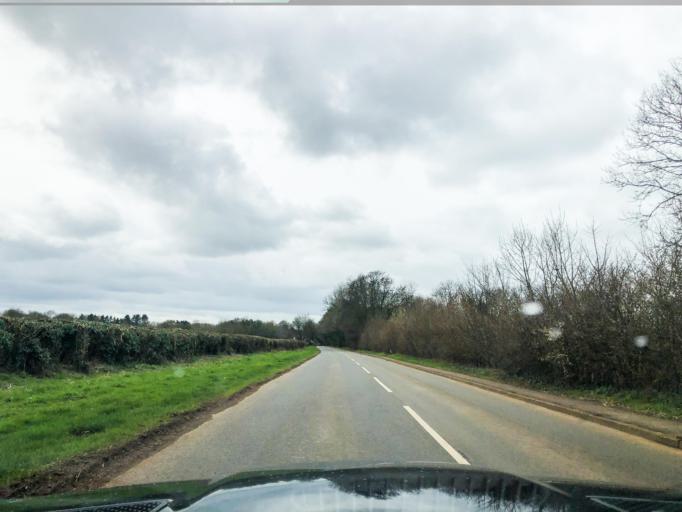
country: GB
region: England
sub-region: Oxfordshire
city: Hanwell
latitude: 52.1270
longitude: -1.4486
